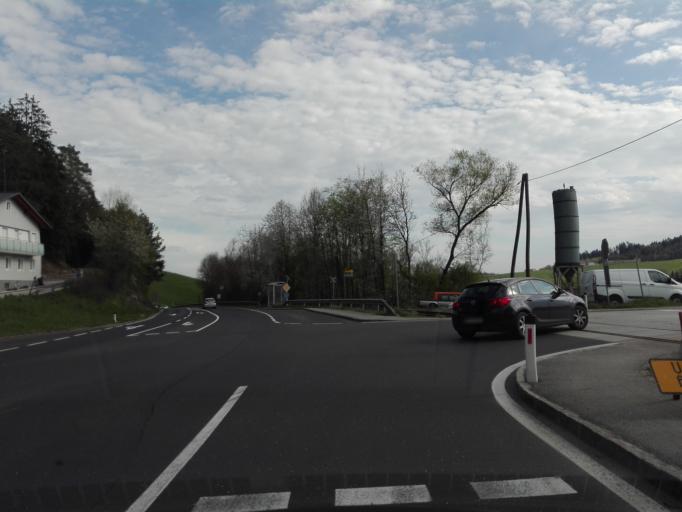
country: AT
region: Upper Austria
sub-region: Politischer Bezirk Urfahr-Umgebung
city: Sankt Gotthard im Muhlkreis
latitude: 48.3859
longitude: 14.0915
